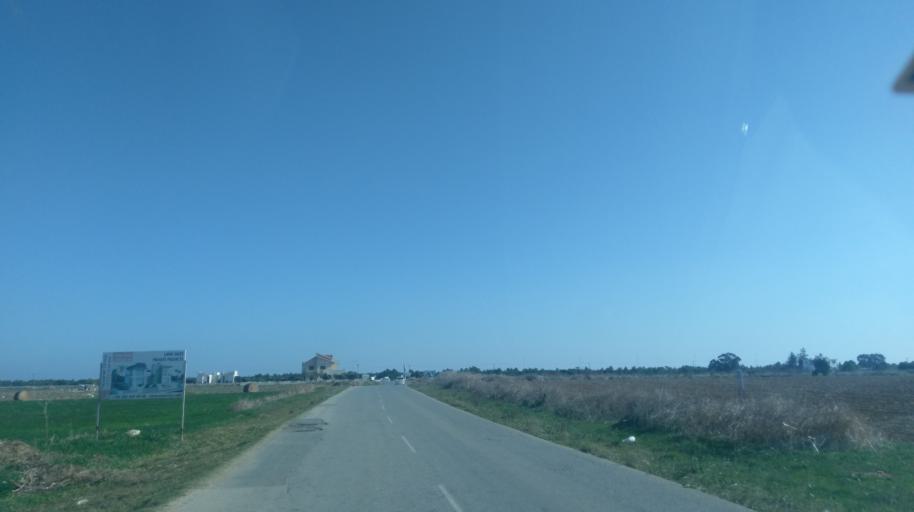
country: CY
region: Ammochostos
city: Trikomo
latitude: 35.2308
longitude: 33.8930
